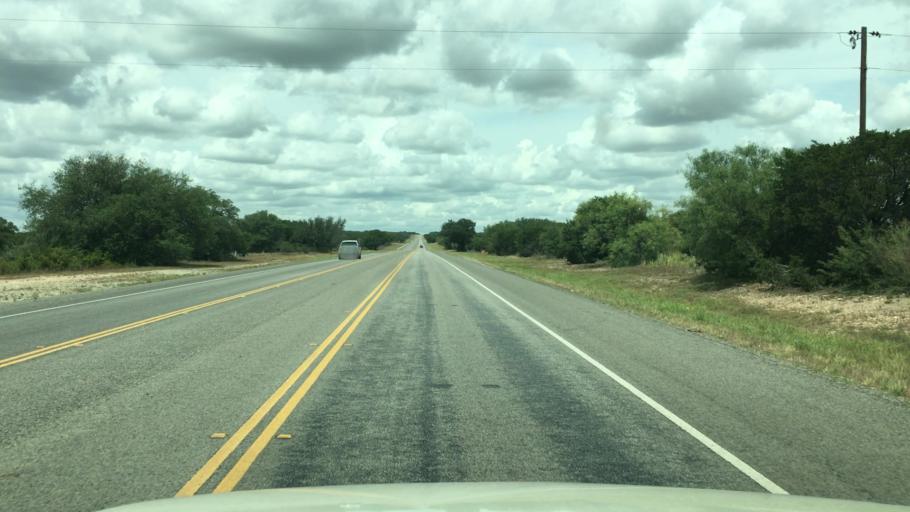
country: US
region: Texas
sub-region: McCulloch County
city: Brady
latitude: 31.0203
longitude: -99.2144
